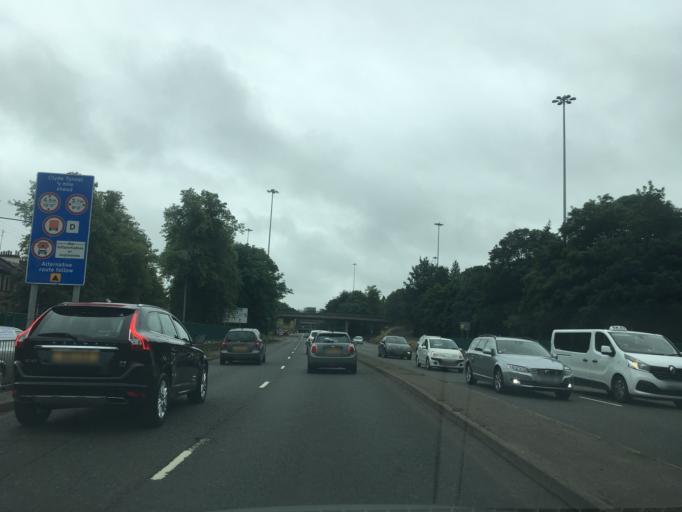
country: GB
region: Scotland
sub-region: East Dunbartonshire
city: Bearsden
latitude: 55.8764
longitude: -4.3270
